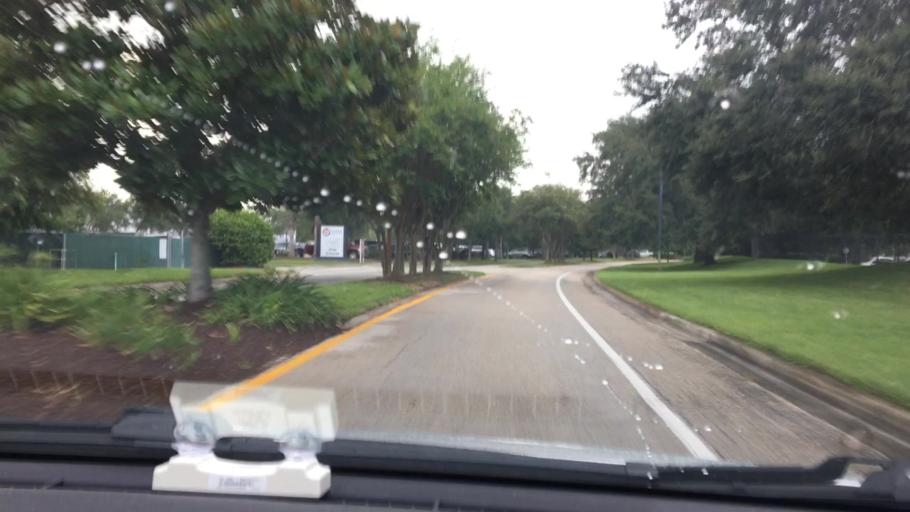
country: US
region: Florida
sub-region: Orange County
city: Conway
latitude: 28.4719
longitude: -81.3074
